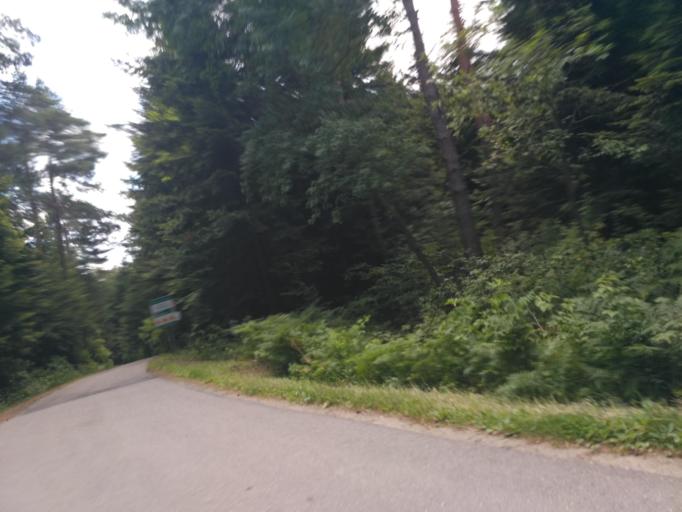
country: PL
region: Subcarpathian Voivodeship
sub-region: Powiat jasielski
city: Brzyska
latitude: 49.8071
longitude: 21.3802
